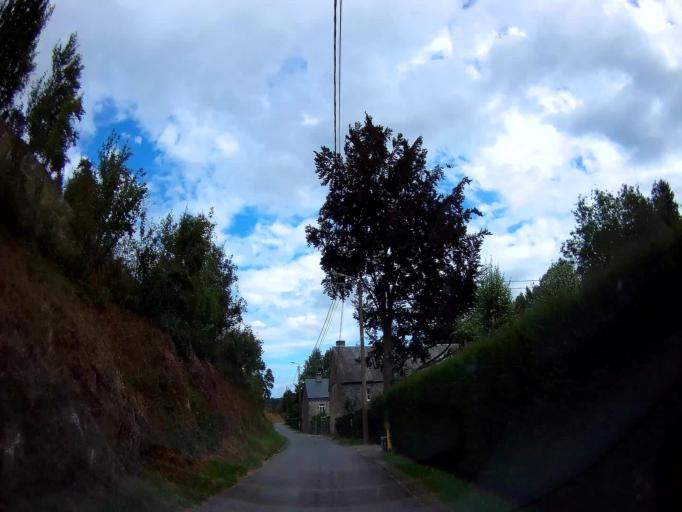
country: BE
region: Wallonia
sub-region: Province de Liege
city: Hamoir
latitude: 50.3931
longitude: 5.5397
